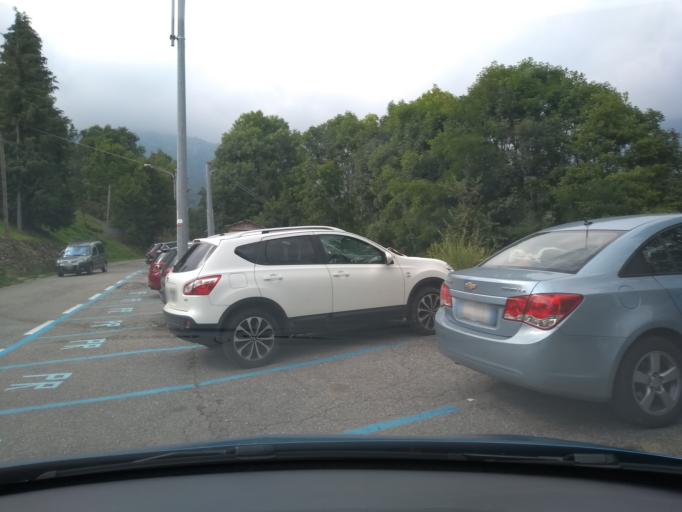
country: IT
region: Piedmont
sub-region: Provincia di Torino
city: Corio
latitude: 45.3370
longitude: 7.5179
